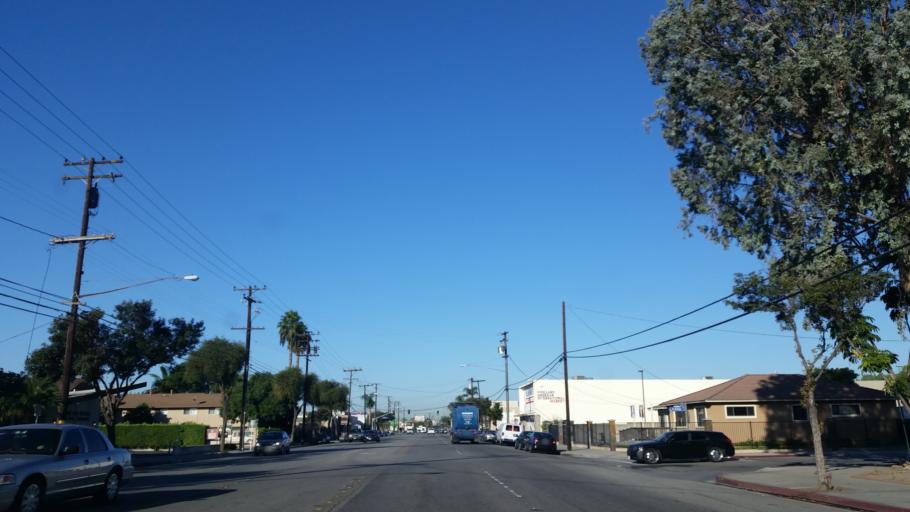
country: US
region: California
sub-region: Los Angeles County
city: Bellflower
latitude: 33.8729
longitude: -118.1125
